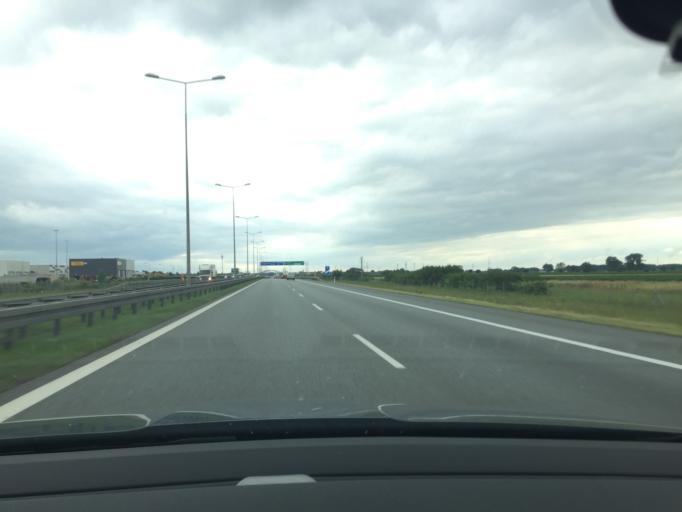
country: PL
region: Greater Poland Voivodeship
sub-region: Powiat poznanski
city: Komorniki
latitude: 52.3505
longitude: 16.7895
